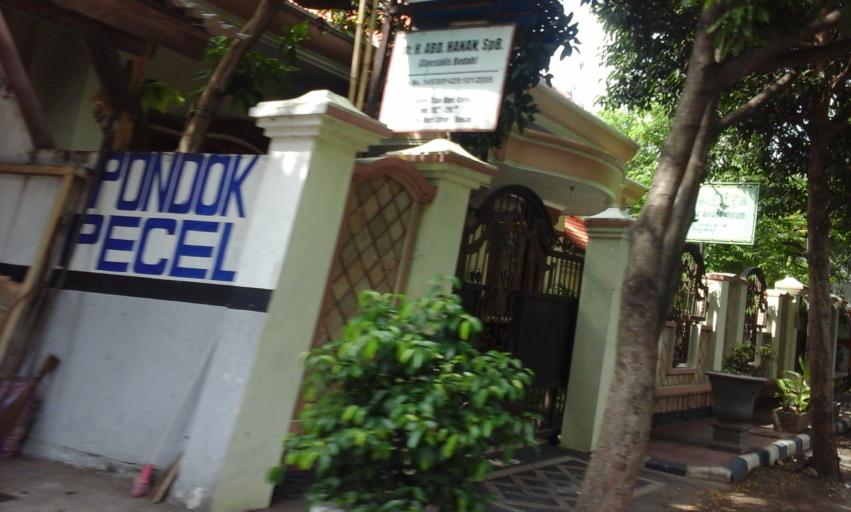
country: ID
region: East Java
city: Krajan
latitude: -8.2276
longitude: 114.3654
